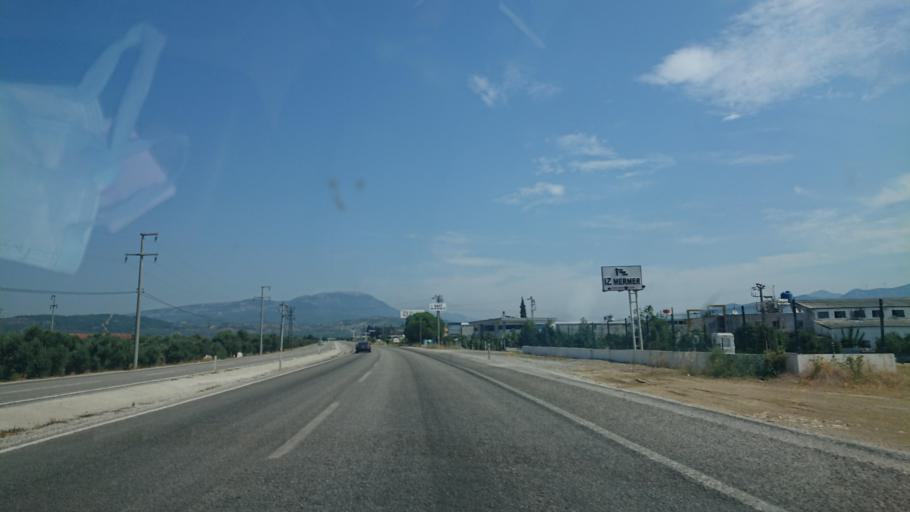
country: TR
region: Izmir
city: Torbali
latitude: 38.2199
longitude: 27.3703
